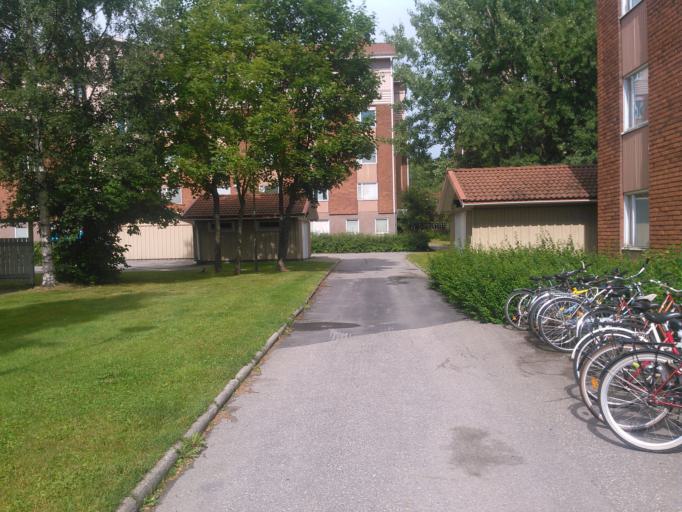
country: SE
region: Vaesterbotten
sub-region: Umea Kommun
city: Umea
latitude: 63.8125
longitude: 20.3101
